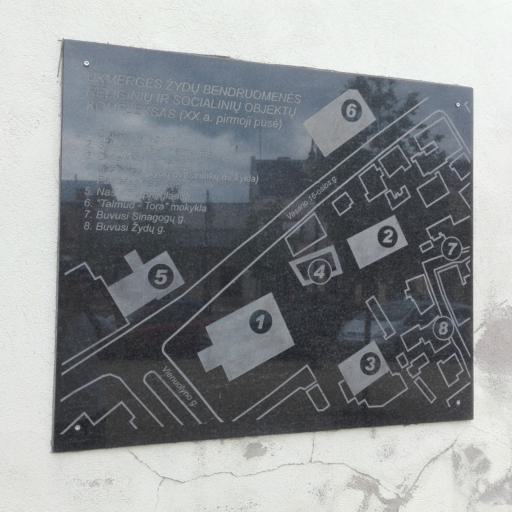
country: LT
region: Vilnius County
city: Ukmerge
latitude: 55.2510
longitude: 24.7613
